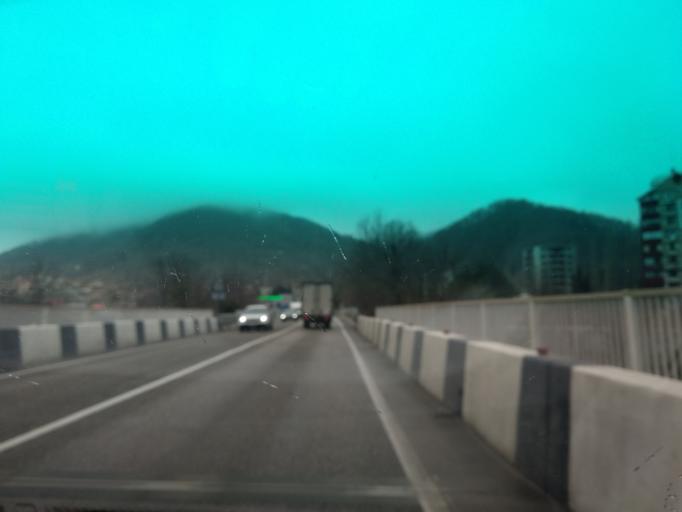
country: RU
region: Krasnodarskiy
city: Agoy
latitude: 44.1459
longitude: 39.0419
